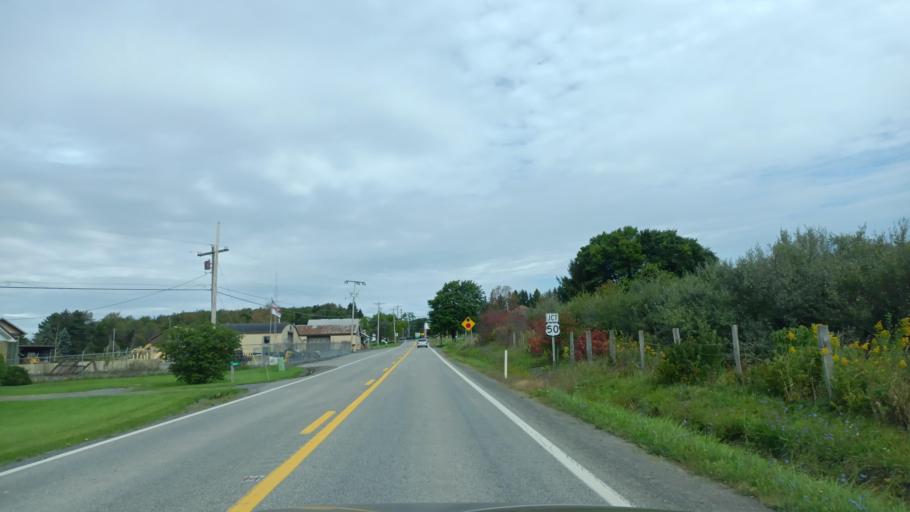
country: US
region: Maryland
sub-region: Garrett County
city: Mountain Lake Park
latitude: 39.2747
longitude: -79.2401
